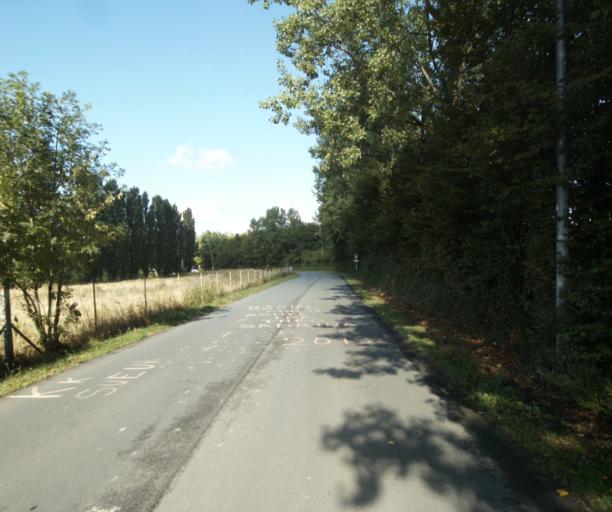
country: FR
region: Nord-Pas-de-Calais
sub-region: Departement du Nord
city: Hem
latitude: 50.6458
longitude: 3.1980
